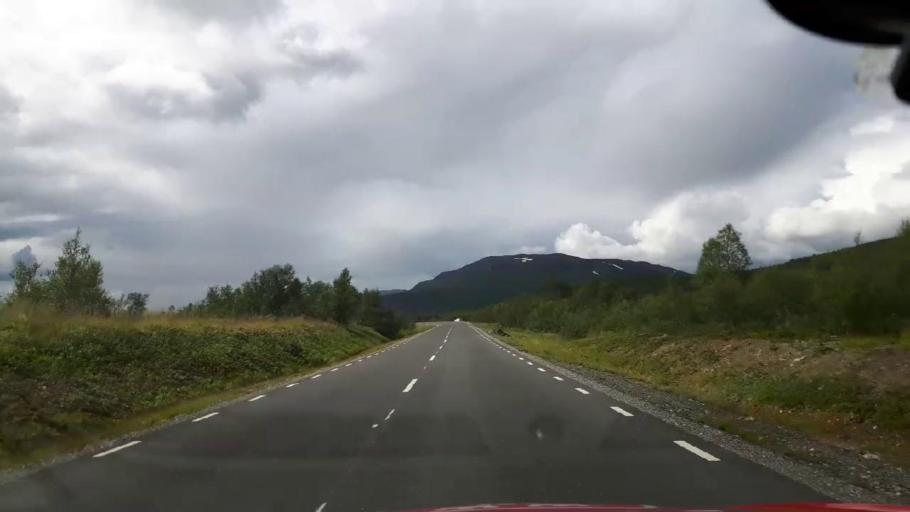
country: NO
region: Nordland
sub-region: Hattfjelldal
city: Hattfjelldal
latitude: 65.0016
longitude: 14.2472
